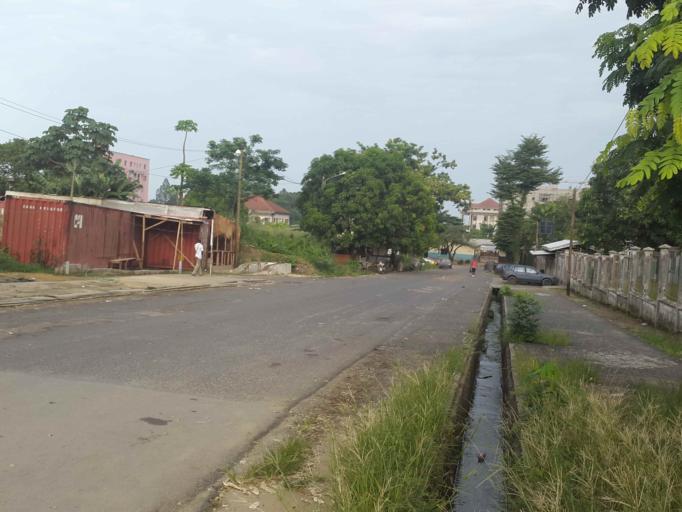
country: CM
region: Littoral
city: Douala
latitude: 4.0912
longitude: 9.7410
